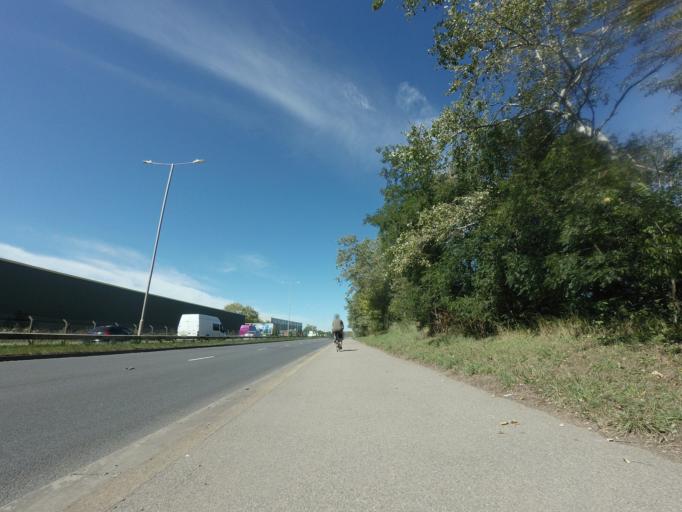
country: GB
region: England
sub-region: Kent
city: Sandwich
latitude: 51.3066
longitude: 1.3479
